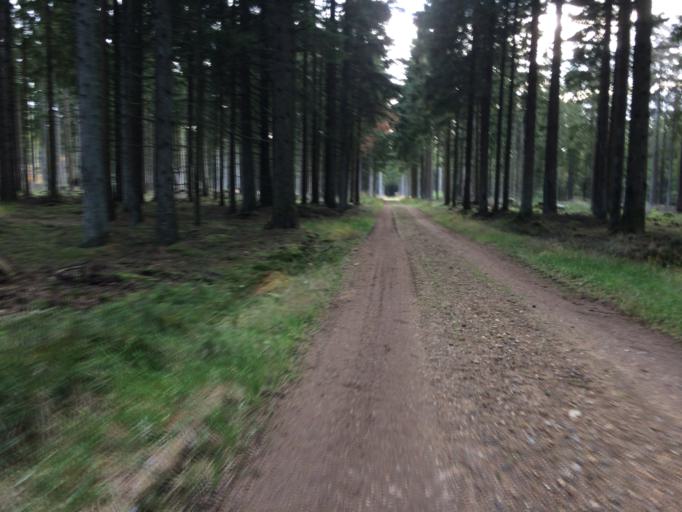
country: DK
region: Central Jutland
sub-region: Holstebro Kommune
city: Ulfborg
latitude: 56.2100
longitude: 8.4602
